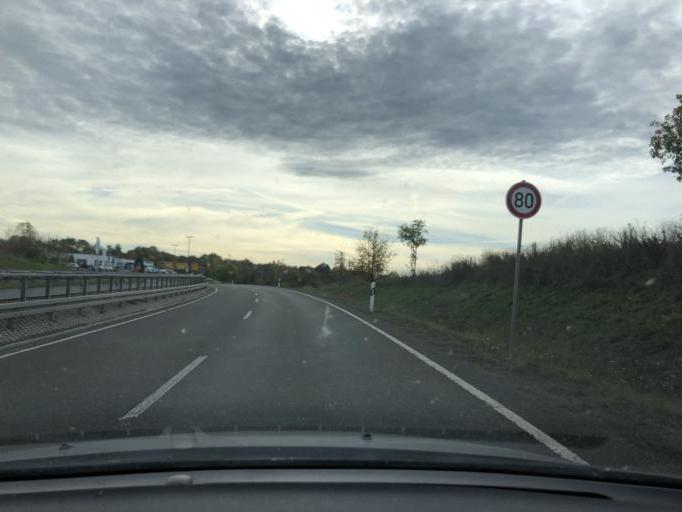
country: DE
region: Thuringia
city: Gera
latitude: 50.8834
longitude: 12.1142
